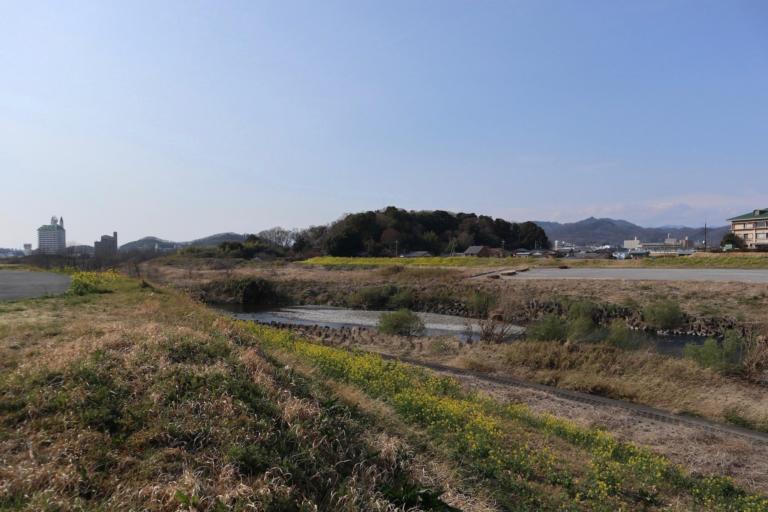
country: JP
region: Tochigi
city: Ashikaga
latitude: 36.3195
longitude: 139.4627
